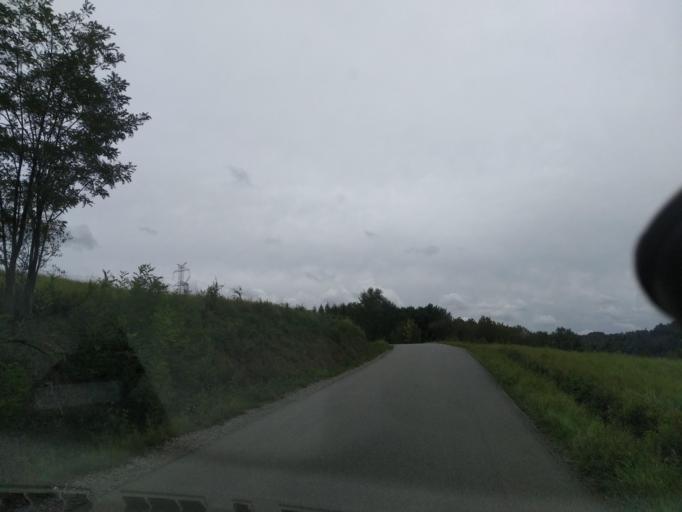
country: PL
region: Subcarpathian Voivodeship
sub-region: Powiat krosnienski
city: Iwonicz-Zdroj
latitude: 49.5399
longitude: 21.7444
